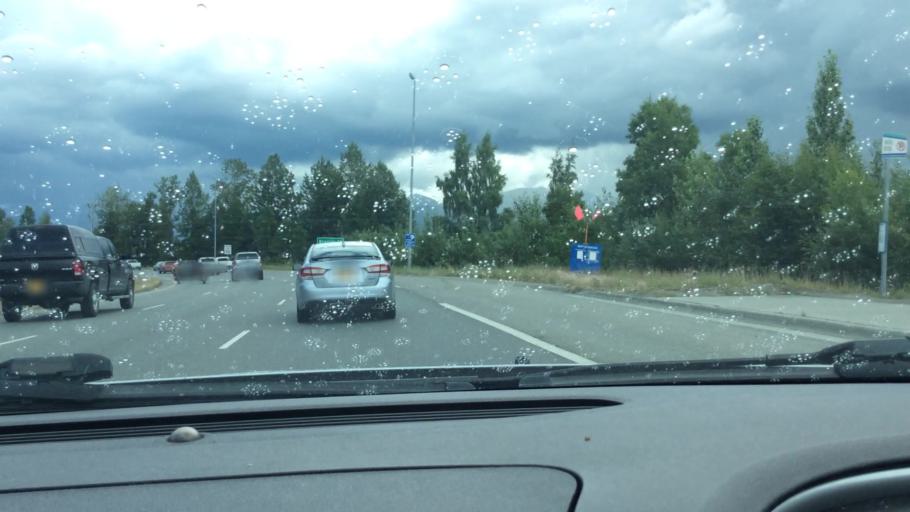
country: US
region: Alaska
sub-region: Anchorage Municipality
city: Anchorage
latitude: 61.2175
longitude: -149.8246
